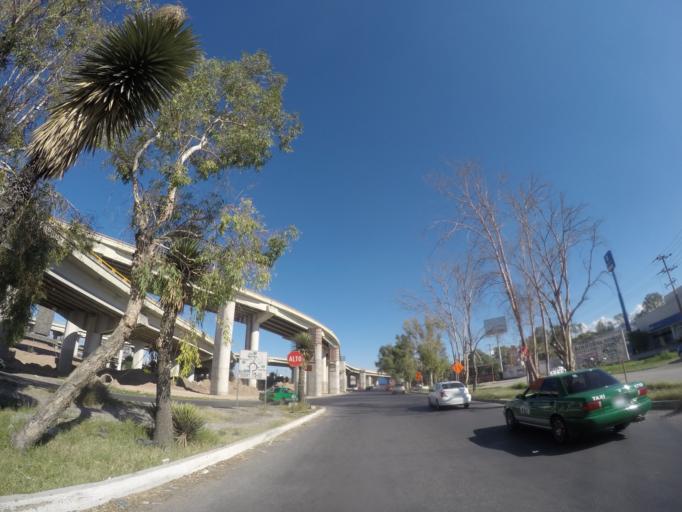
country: MX
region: San Luis Potosi
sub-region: San Luis Potosi
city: San Luis Potosi
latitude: 22.1508
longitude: -100.9576
